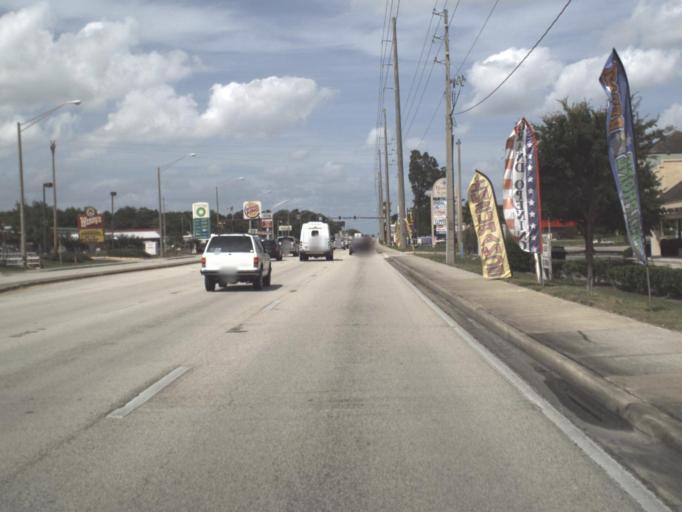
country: US
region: Florida
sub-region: Clay County
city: Lakeside
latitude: 30.1312
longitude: -81.7852
